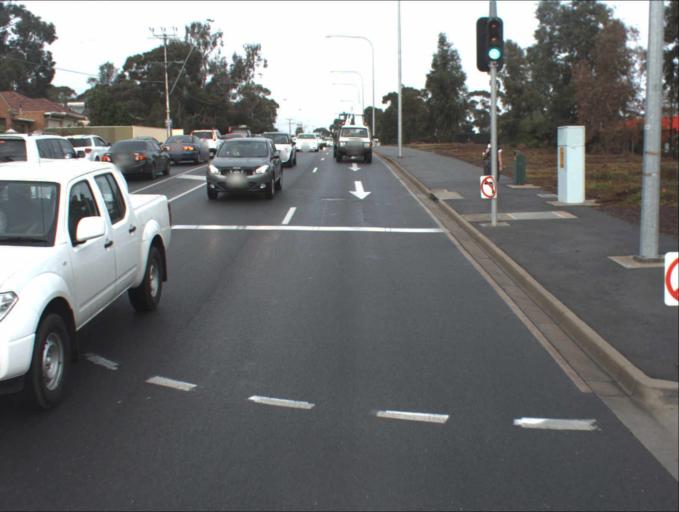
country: AU
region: South Australia
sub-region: Salisbury
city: Ingle Farm
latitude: -34.8430
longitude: 138.6203
